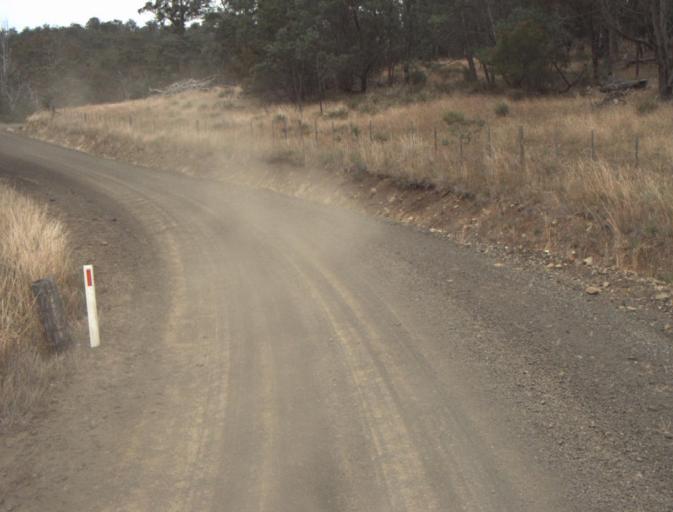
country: AU
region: Tasmania
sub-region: Northern Midlands
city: Evandale
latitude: -41.5169
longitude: 147.3818
